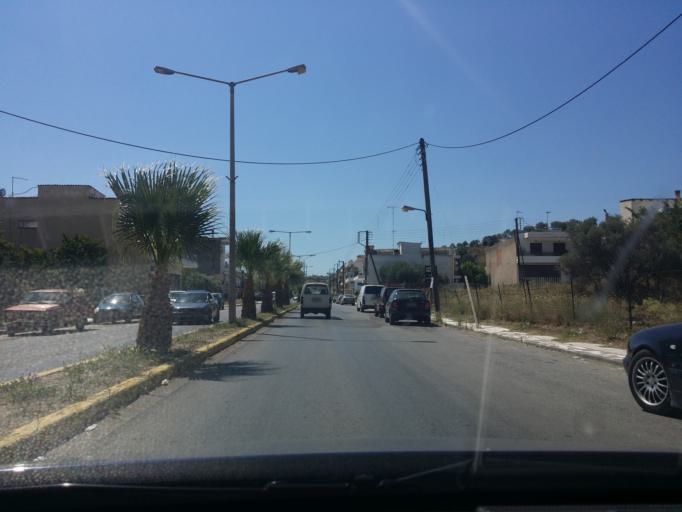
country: GR
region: Peloponnese
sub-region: Nomos Lakonias
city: Sparti
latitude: 37.0849
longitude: 22.4311
